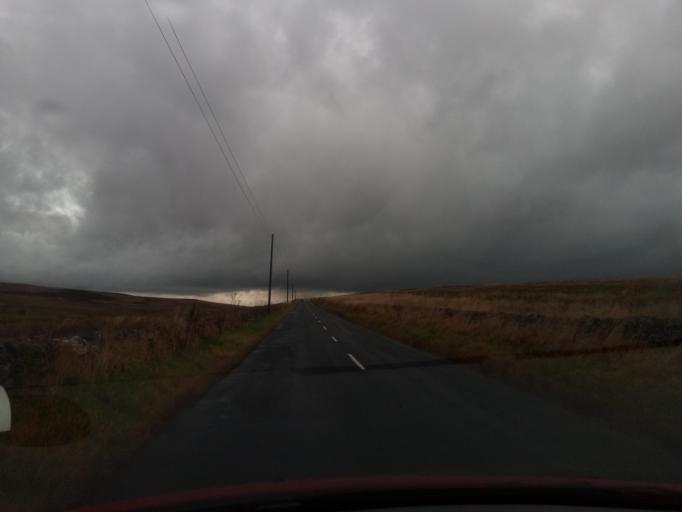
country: GB
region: England
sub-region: Northumberland
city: Rochester
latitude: 55.1799
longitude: -2.2627
